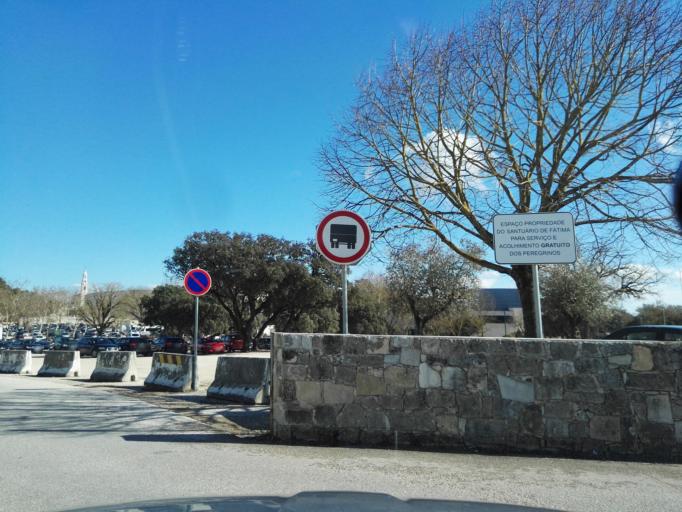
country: PT
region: Santarem
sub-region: Ourem
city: Fatima
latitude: 39.6276
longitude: -8.6799
